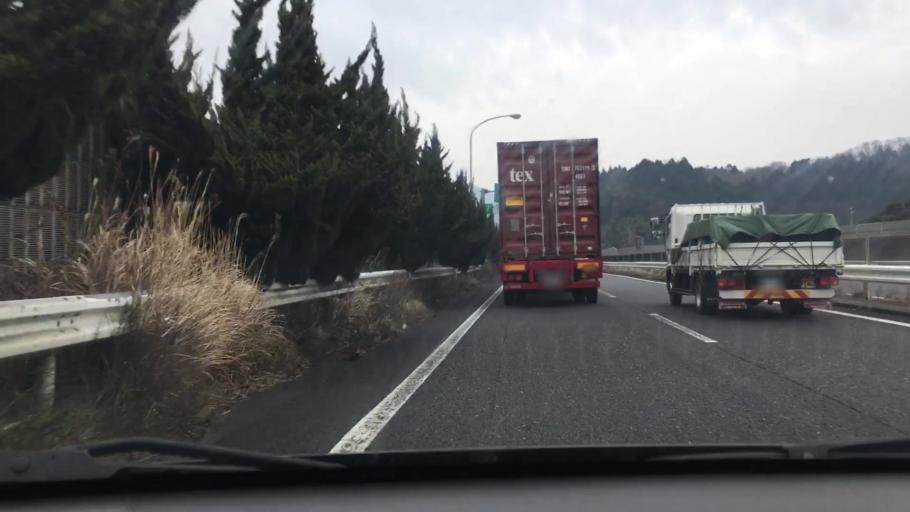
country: JP
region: Mie
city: Ueno-ebisumachi
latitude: 34.8339
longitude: 136.2441
